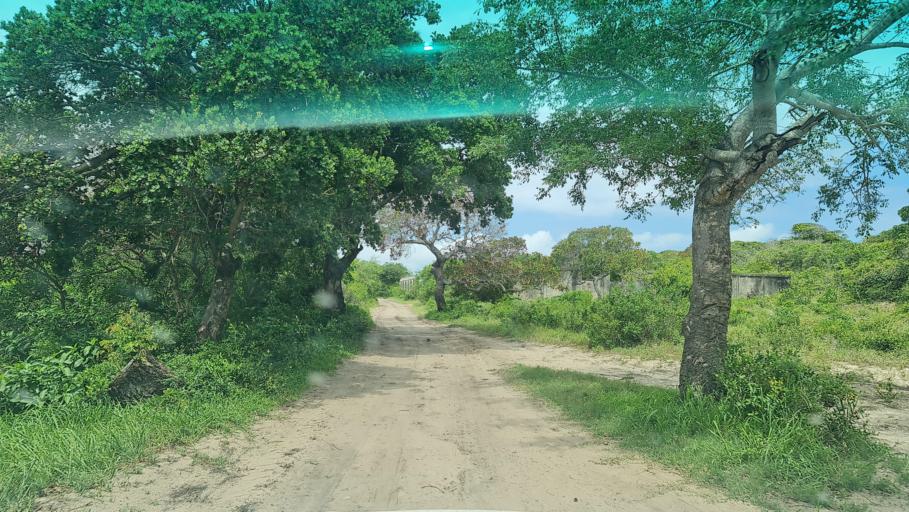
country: MZ
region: Maputo
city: Manhica
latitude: -25.5198
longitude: 32.8698
